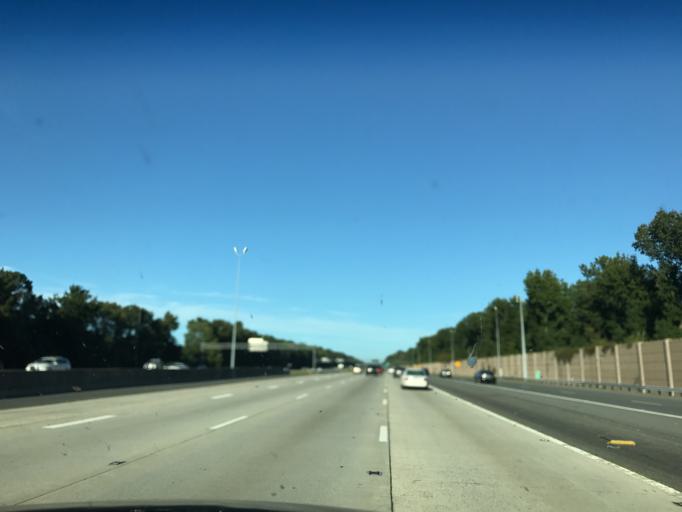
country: US
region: Virginia
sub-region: City of Chesapeake
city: Chesapeake
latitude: 36.7874
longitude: -76.2270
